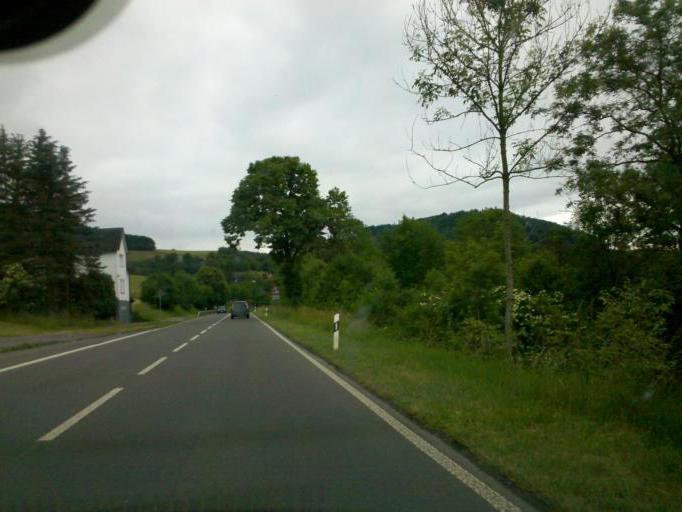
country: DE
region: North Rhine-Westphalia
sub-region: Regierungsbezirk Arnsberg
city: Lennestadt
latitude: 51.1499
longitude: 8.0722
